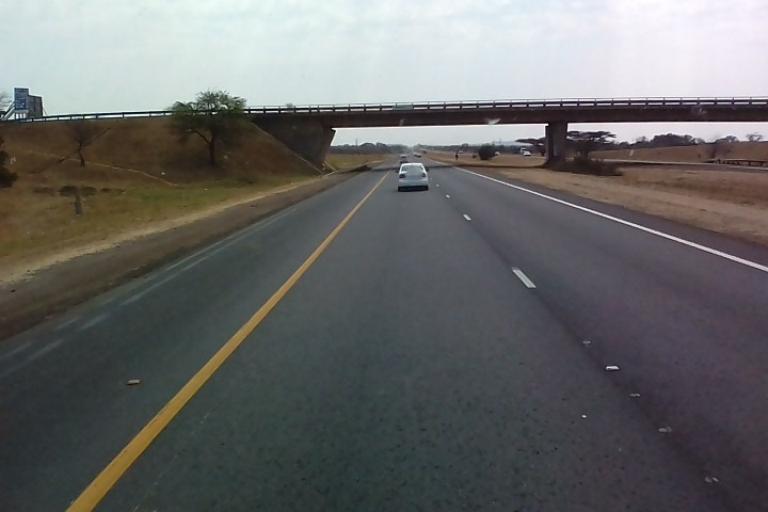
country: ZA
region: Limpopo
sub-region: Waterberg District Municipality
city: Bela-Bela
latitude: -24.9208
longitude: 28.3719
